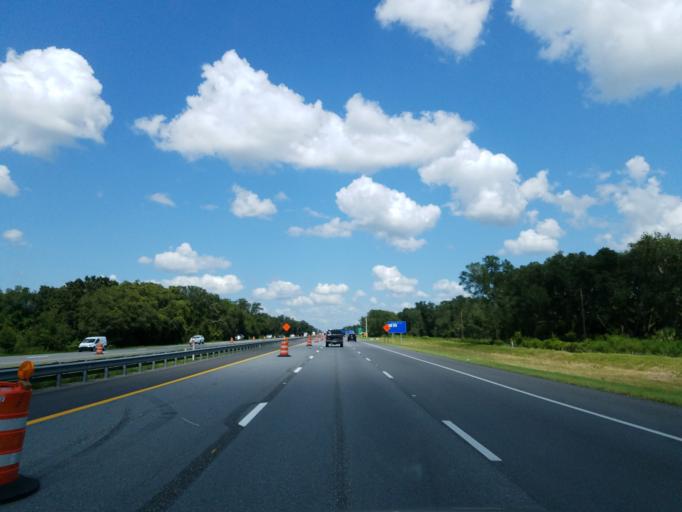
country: US
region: Florida
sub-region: Sumter County
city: Bushnell
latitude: 28.6479
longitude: -82.1569
